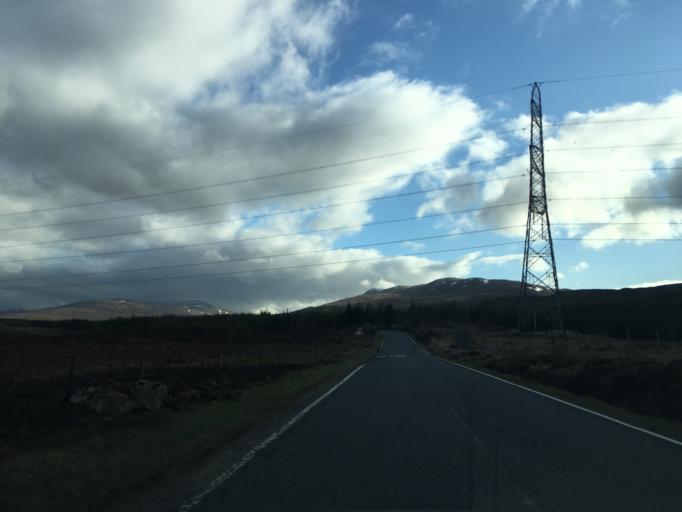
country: GB
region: Scotland
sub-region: Highland
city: Kingussie
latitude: 56.9633
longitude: -4.2423
